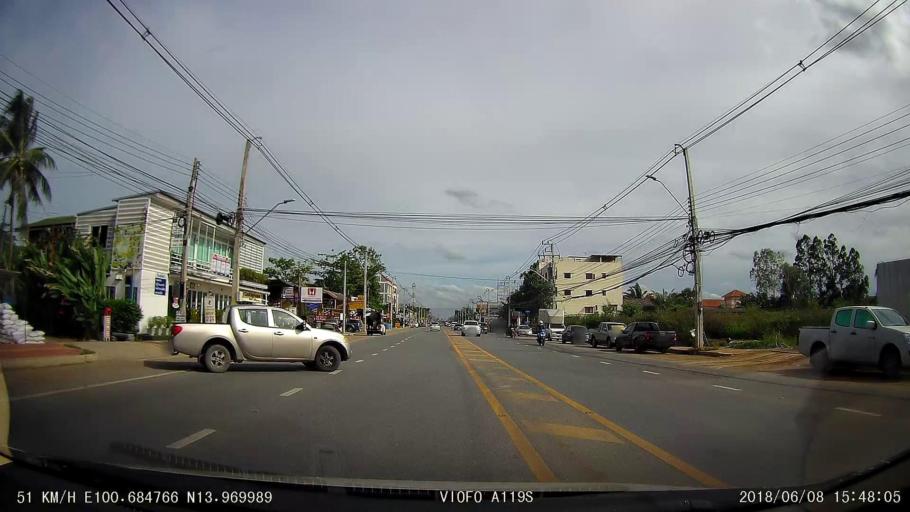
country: TH
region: Bangkok
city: Sai Mai
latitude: 13.9700
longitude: 100.6848
